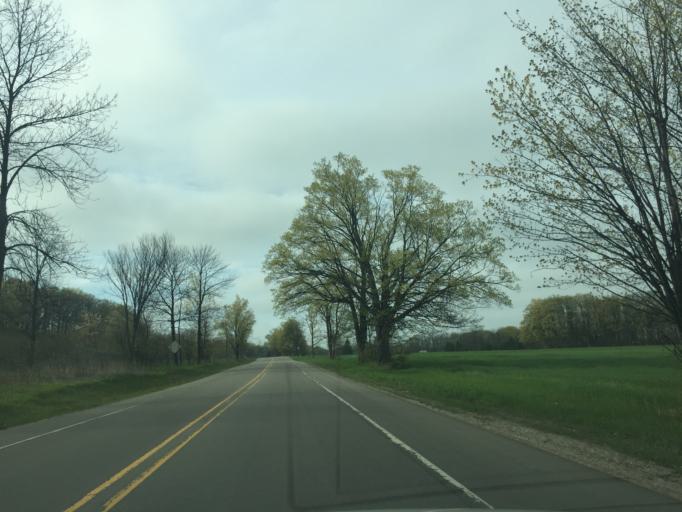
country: US
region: Michigan
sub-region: Leelanau County
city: Leland
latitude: 45.0710
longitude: -85.5877
